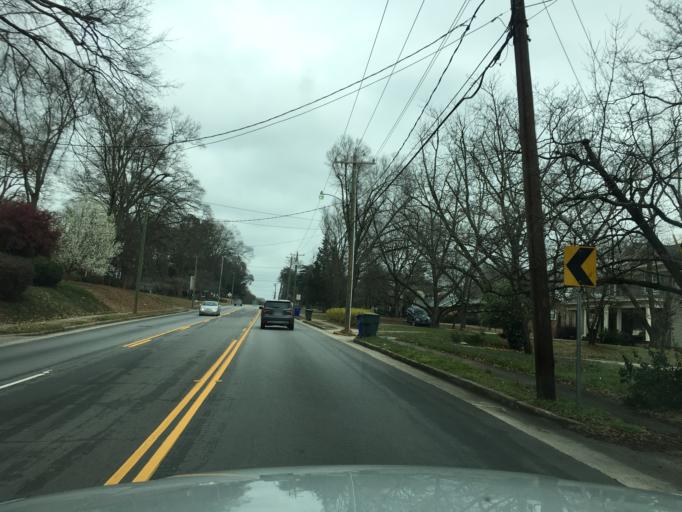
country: US
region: South Carolina
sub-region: Greenville County
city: Greenville
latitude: 34.8611
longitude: -82.3713
